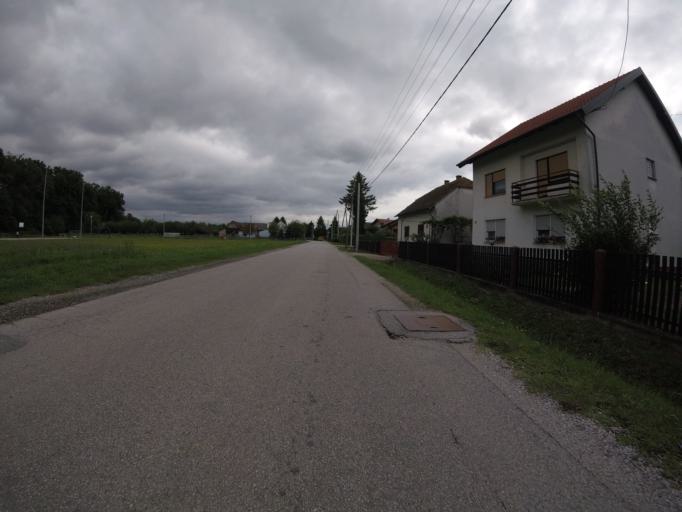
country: HR
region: Zagrebacka
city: Gradici
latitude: 45.6947
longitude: 16.0333
